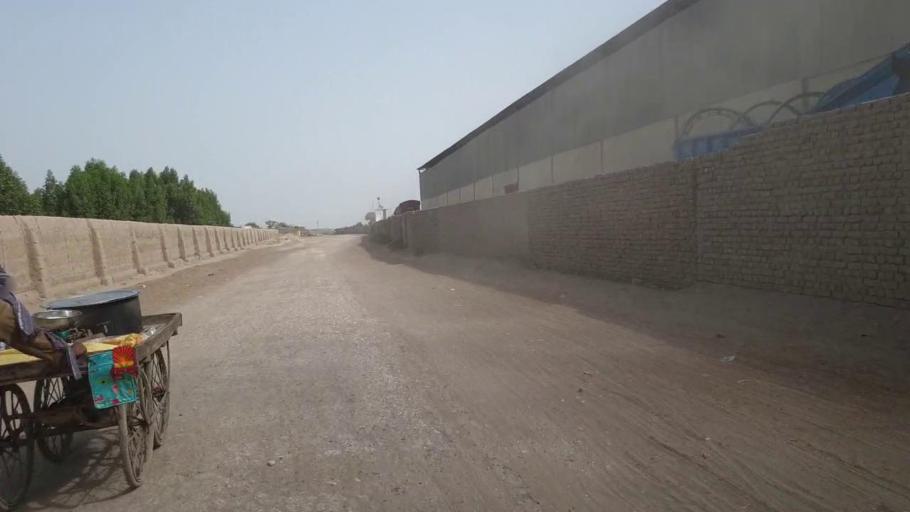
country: PK
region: Sindh
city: Daulatpur
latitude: 26.5572
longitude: 67.9892
